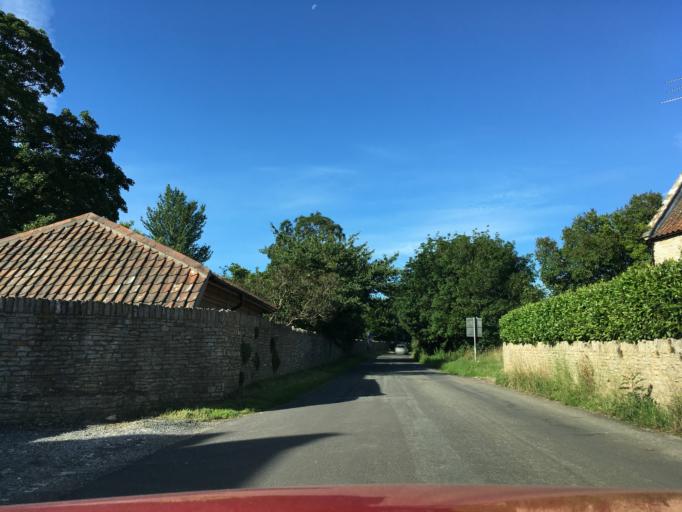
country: GB
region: England
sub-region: Bath and North East Somerset
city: Compton Dando
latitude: 51.4007
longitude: -2.5281
